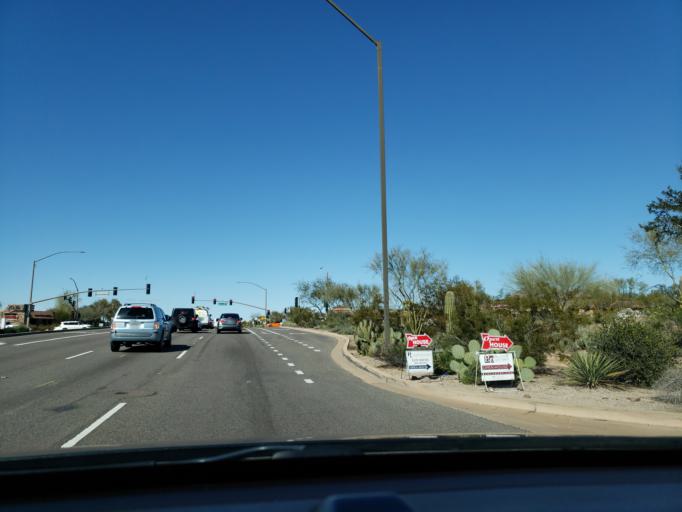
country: US
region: Arizona
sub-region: Maricopa County
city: Carefree
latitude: 33.6977
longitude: -111.8905
